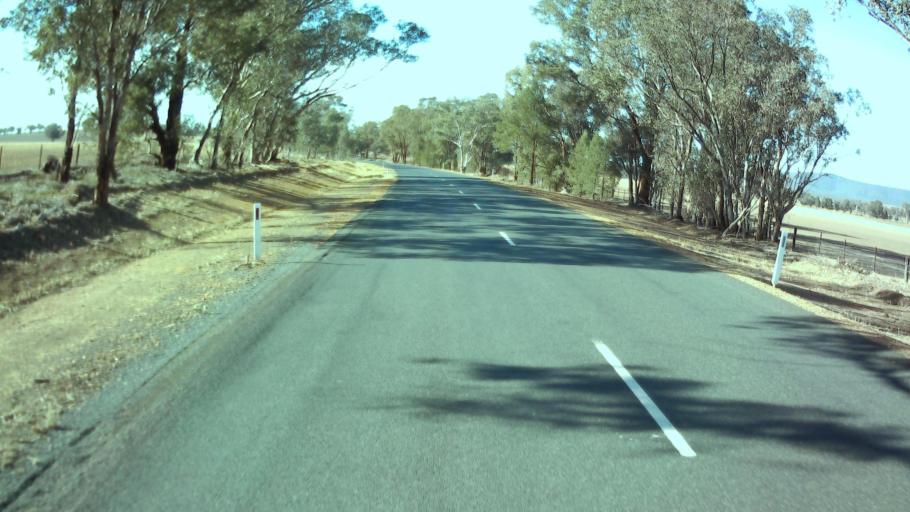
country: AU
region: New South Wales
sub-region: Weddin
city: Grenfell
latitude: -33.9300
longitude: 148.1375
